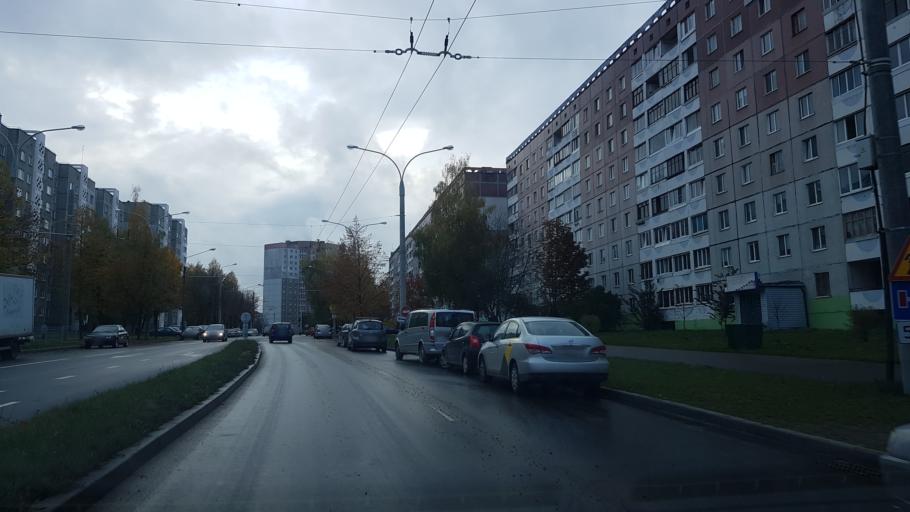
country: BY
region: Minsk
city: Syenitsa
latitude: 53.8513
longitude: 27.5534
